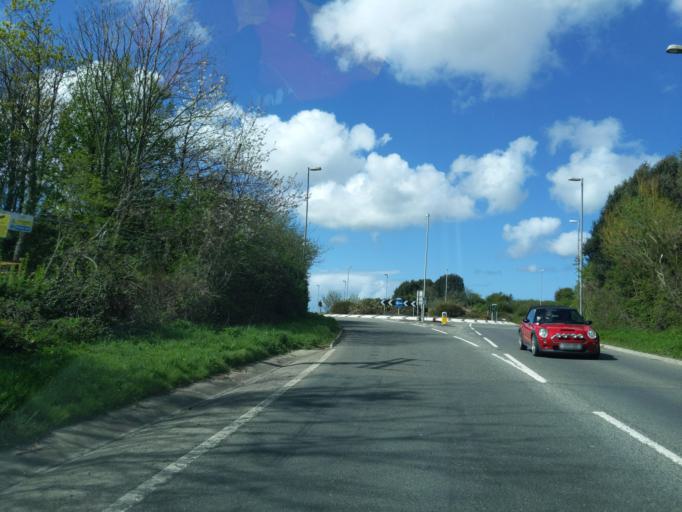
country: GB
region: England
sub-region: Cornwall
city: Wadebridge
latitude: 50.5224
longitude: -4.8214
